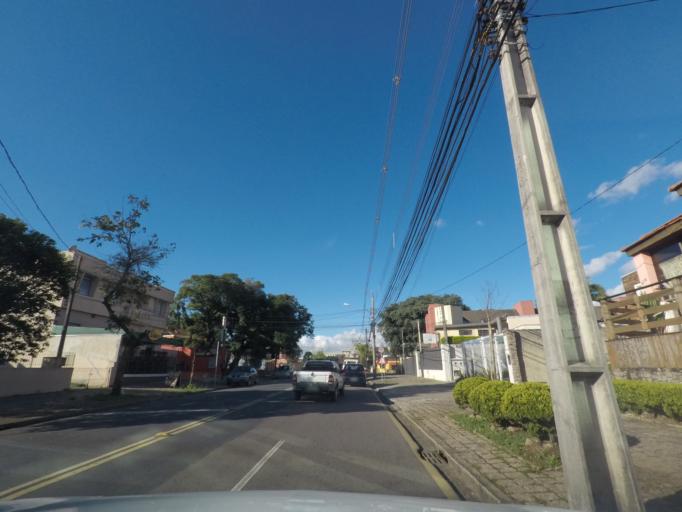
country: BR
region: Parana
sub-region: Curitiba
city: Curitiba
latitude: -25.4232
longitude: -49.2937
